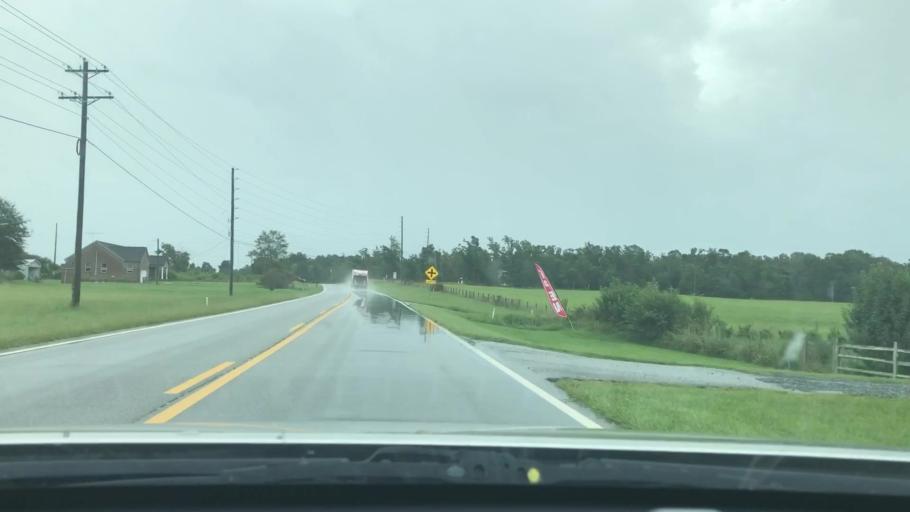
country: US
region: Georgia
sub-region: Lamar County
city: Barnesville
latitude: 33.0600
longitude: -84.2046
